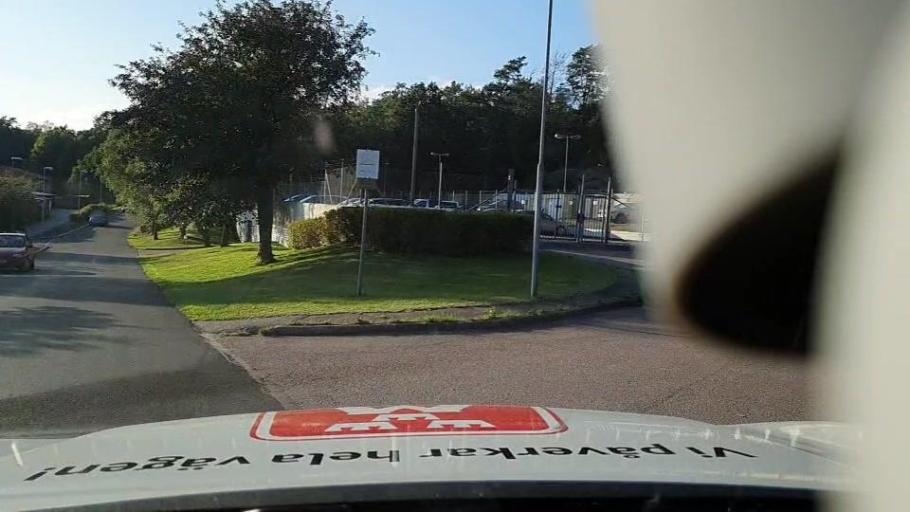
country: SE
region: Vaestra Goetaland
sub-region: Goteborg
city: Loevgaerdet
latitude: 57.8129
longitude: 12.0512
